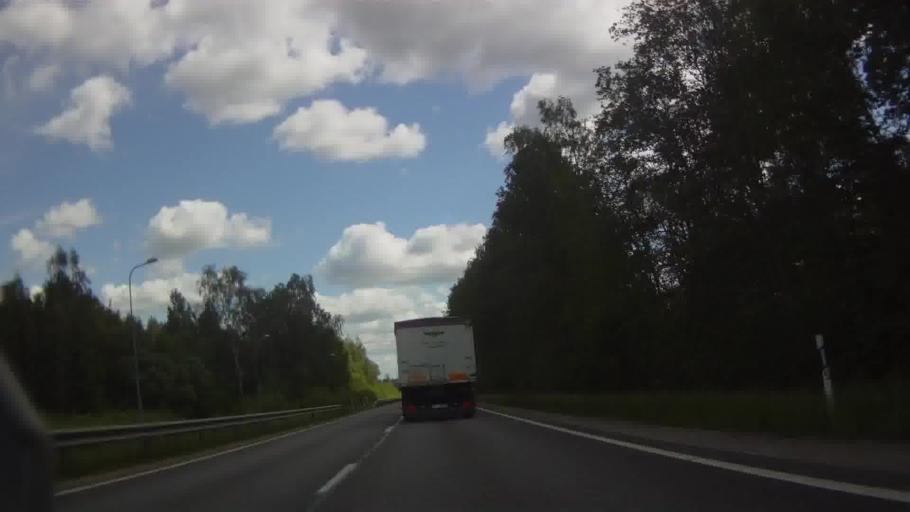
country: LV
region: Livani
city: Livani
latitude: 56.5417
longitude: 26.0760
